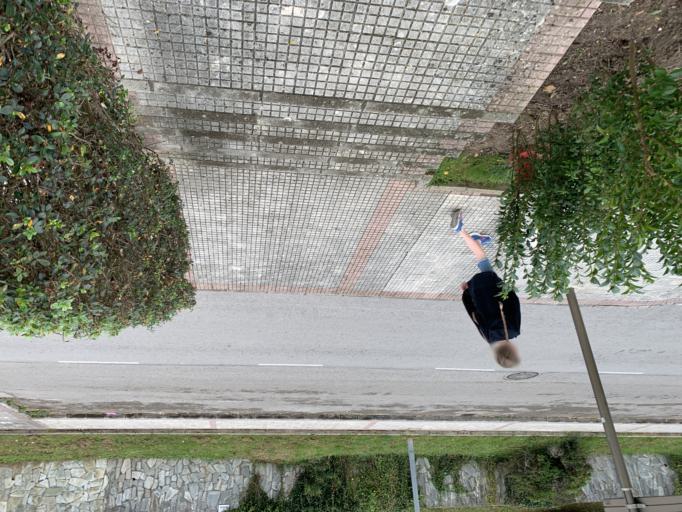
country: ES
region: Cantabria
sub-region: Provincia de Cantabria
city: Comillas
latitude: 43.3856
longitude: -4.2844
